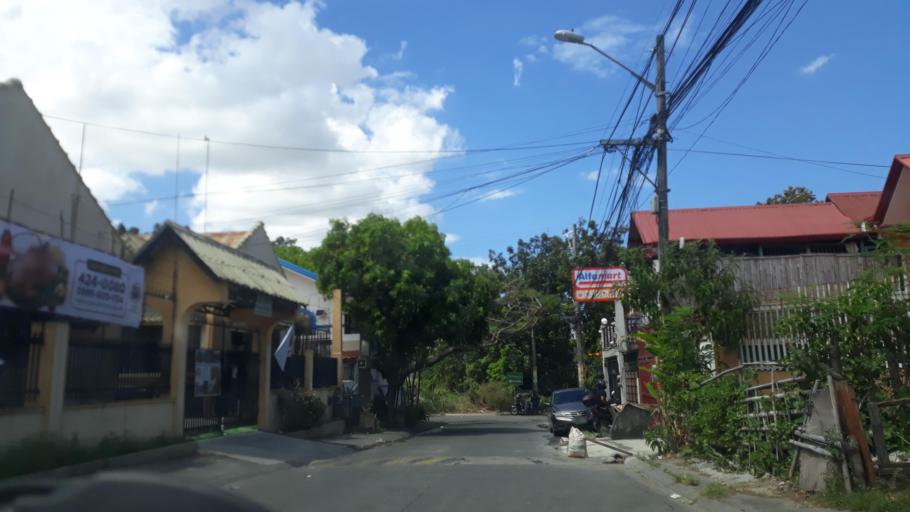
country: PH
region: Calabarzon
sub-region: Province of Cavite
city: Dasmarinas
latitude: 14.3226
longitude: 120.9505
